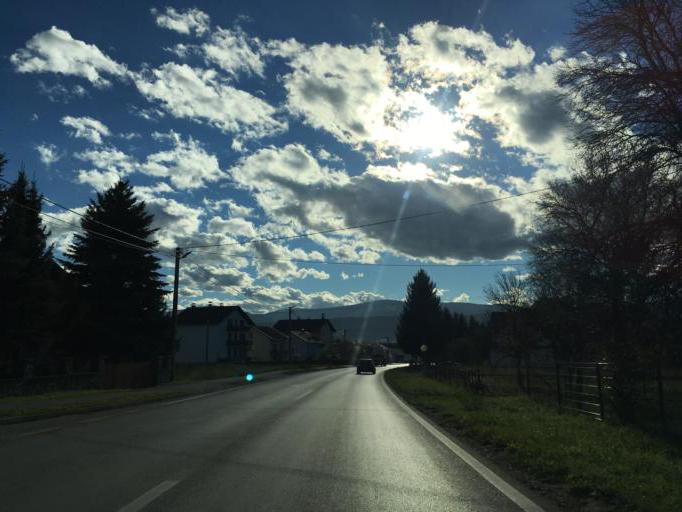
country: BA
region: Federation of Bosnia and Herzegovina
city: Bugojno
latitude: 44.0635
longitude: 17.4712
